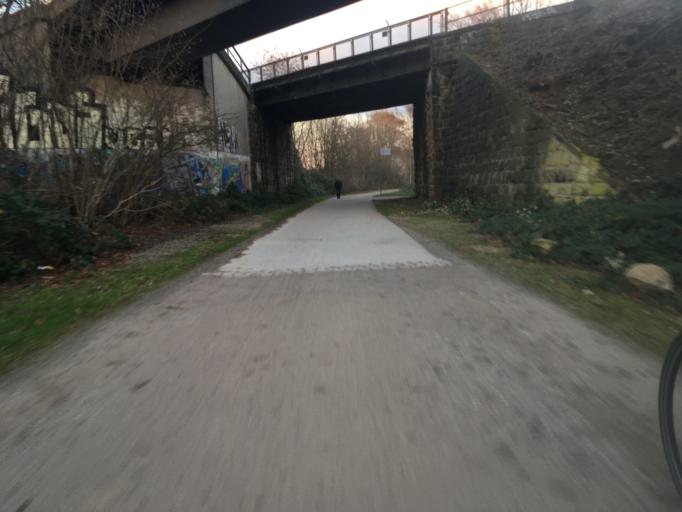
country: DE
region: North Rhine-Westphalia
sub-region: Regierungsbezirk Dusseldorf
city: Essen
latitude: 51.4578
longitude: 6.9536
